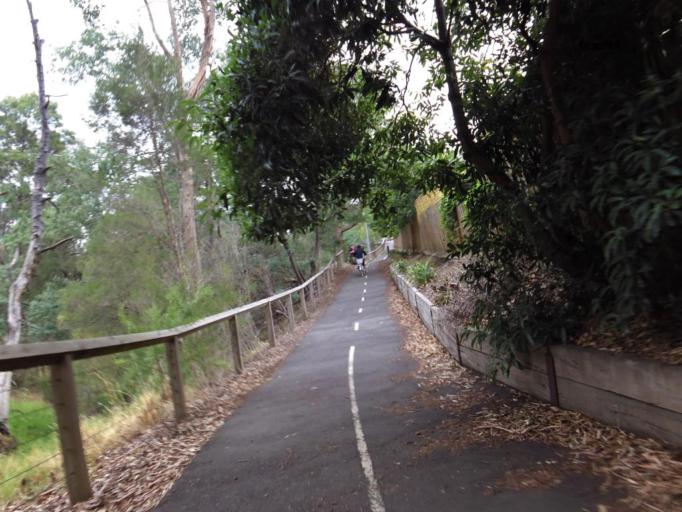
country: AU
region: Victoria
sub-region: Manningham
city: Templestowe Lower
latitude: -37.7702
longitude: 145.1357
